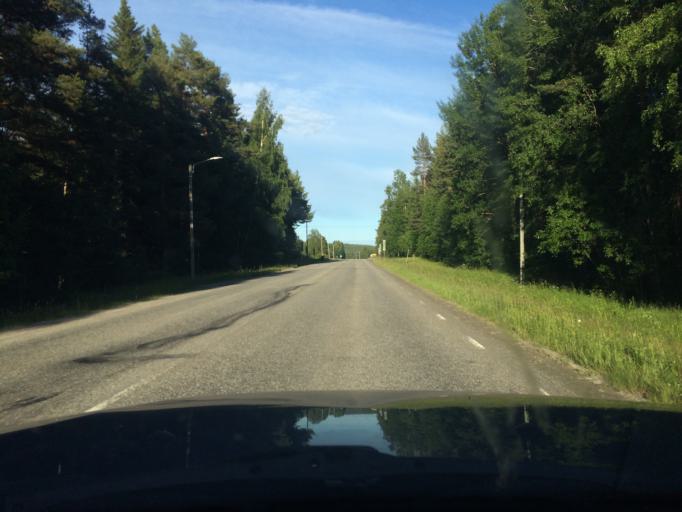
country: SE
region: Norrbotten
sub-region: Pitea Kommun
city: Bergsviken
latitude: 65.3151
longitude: 21.3151
